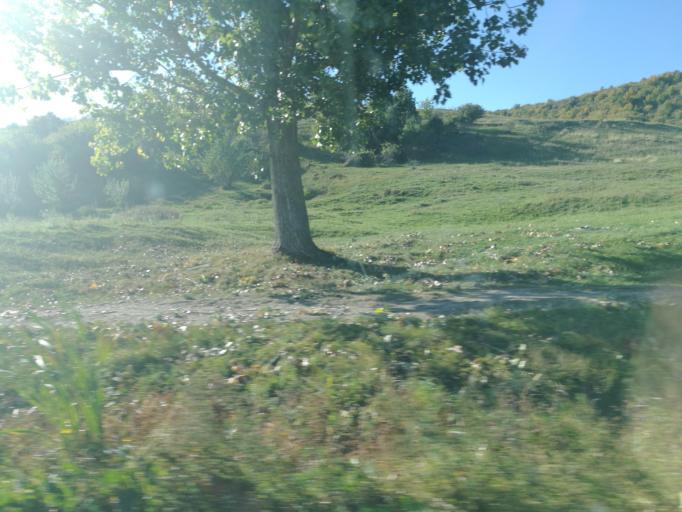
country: RO
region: Brasov
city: Codlea
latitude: 45.7092
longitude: 25.4535
